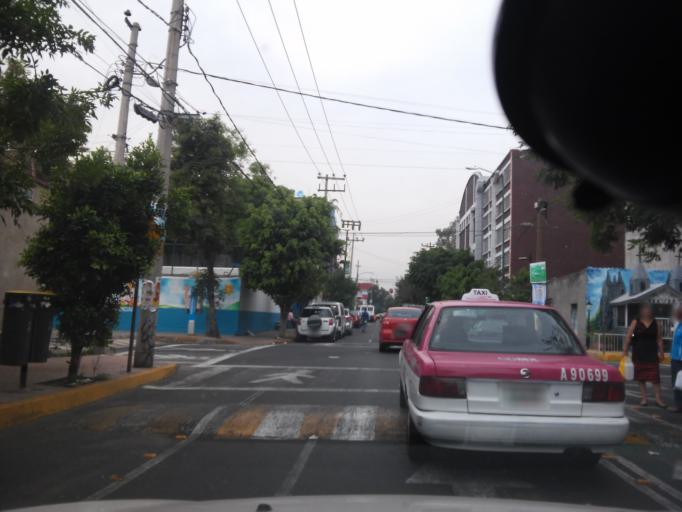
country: MX
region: Mexico City
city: Miguel Hidalgo
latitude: 19.4449
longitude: -99.1783
